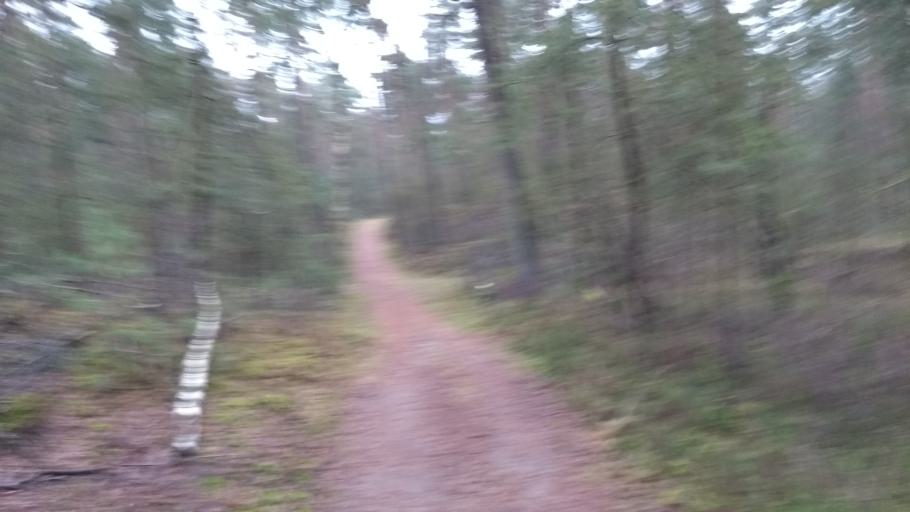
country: NL
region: Gelderland
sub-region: Gemeente Brummen
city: Eerbeek
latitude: 52.0724
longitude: 6.0669
